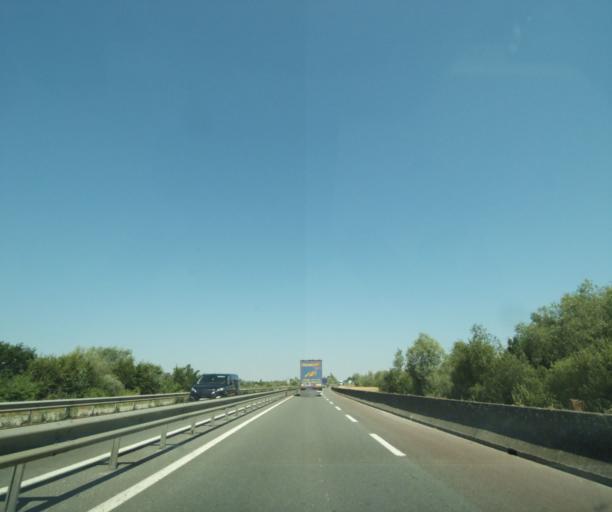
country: FR
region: Champagne-Ardenne
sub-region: Departement de la Haute-Marne
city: Saint-Dizier
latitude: 48.6298
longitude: 4.9286
